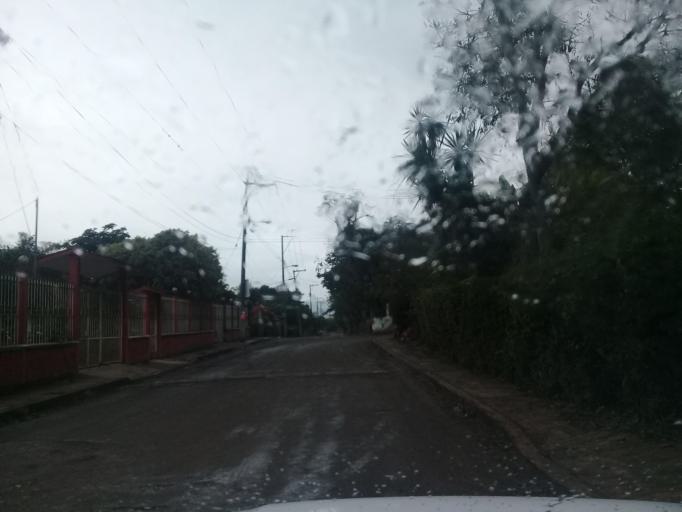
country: MX
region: Veracruz
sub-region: Amatlan de los Reyes
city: Trapiche Viejo
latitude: 18.8442
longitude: -96.9460
